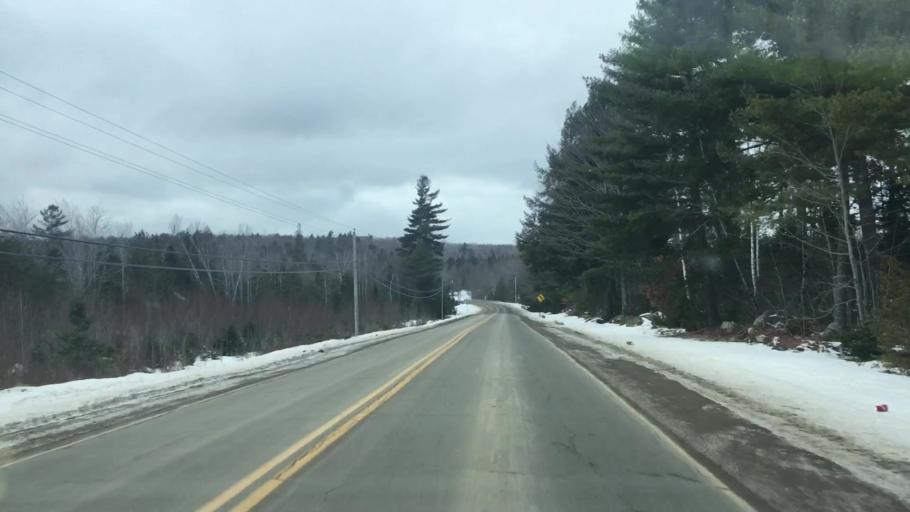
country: US
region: Maine
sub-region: Washington County
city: Calais
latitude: 45.0065
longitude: -67.4123
